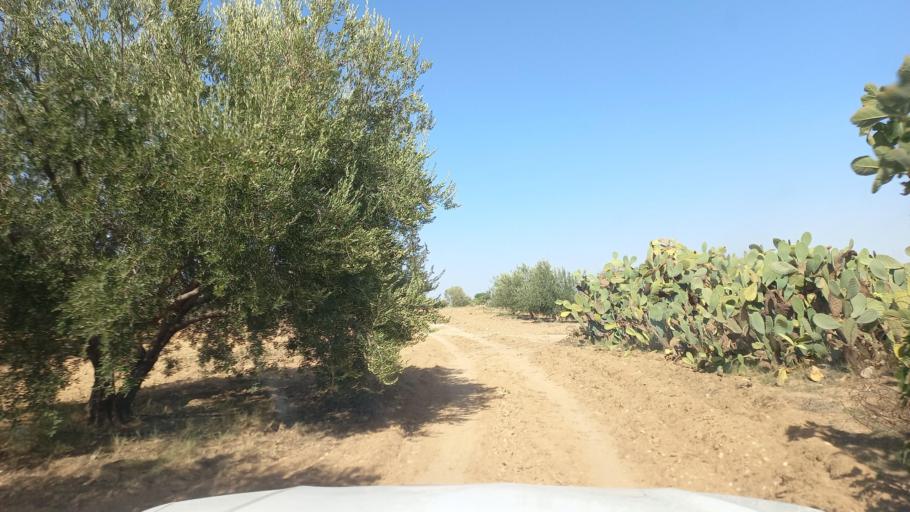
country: TN
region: Al Qasrayn
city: Kasserine
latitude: 35.2712
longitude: 9.0251
